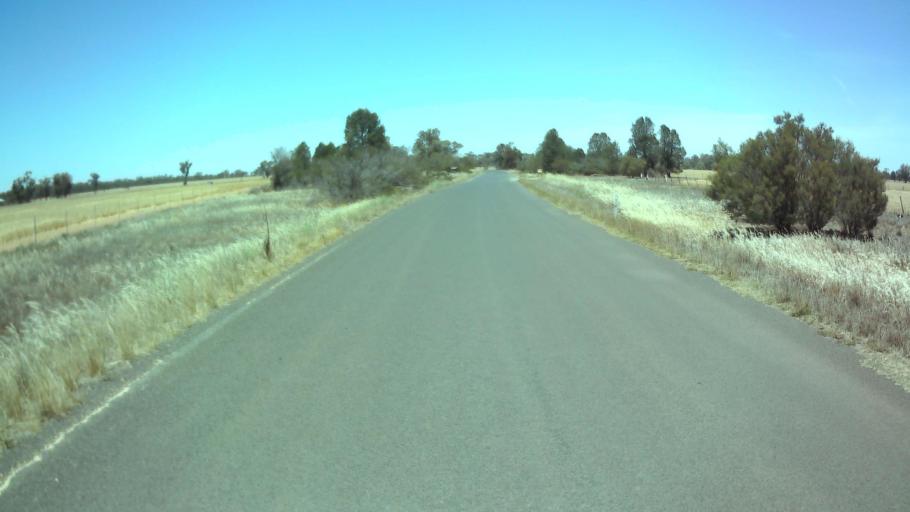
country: AU
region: New South Wales
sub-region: Weddin
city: Grenfell
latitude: -34.0565
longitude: 147.7805
